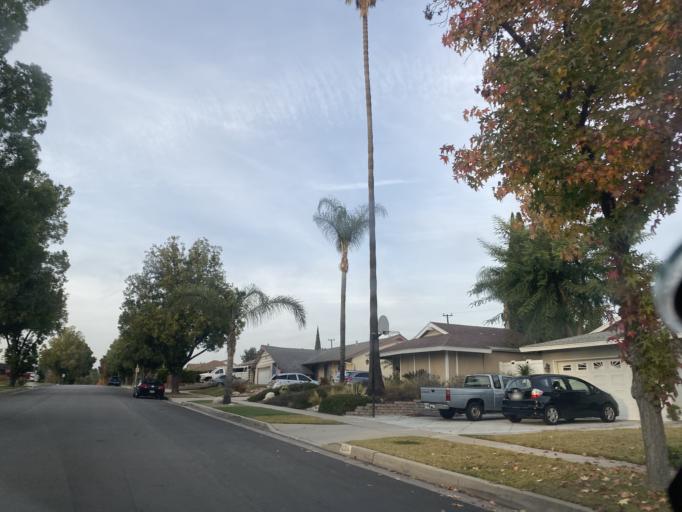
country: US
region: California
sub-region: Orange County
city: Placentia
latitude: 33.8943
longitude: -117.8834
